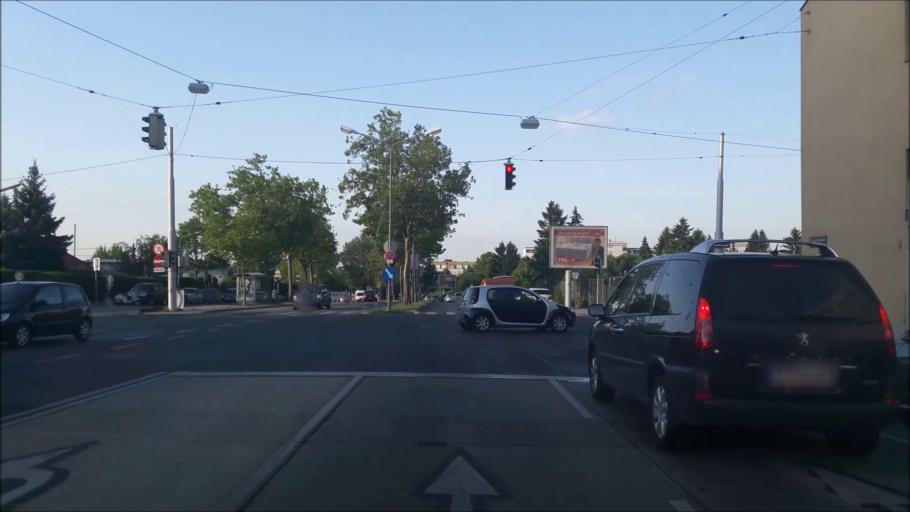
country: AT
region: Vienna
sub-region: Wien Stadt
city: Vienna
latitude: 48.1634
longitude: 16.3675
